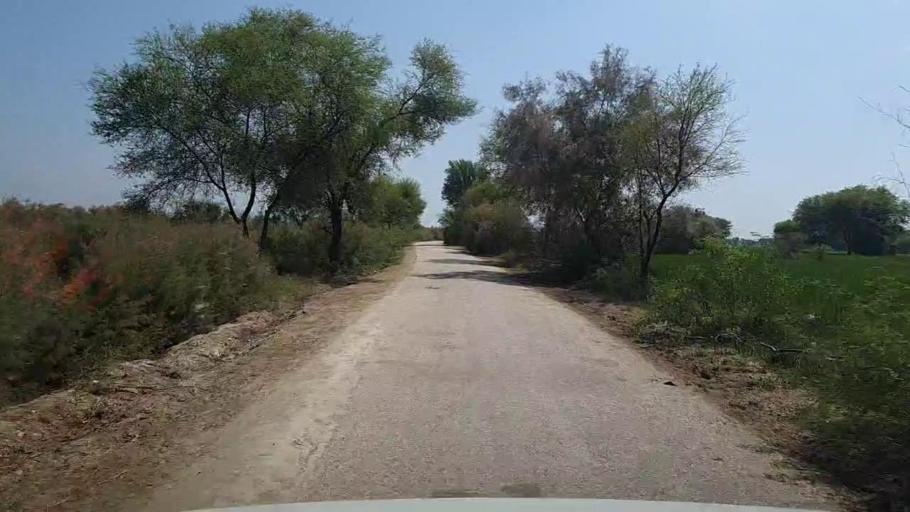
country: PK
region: Sindh
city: Kandhkot
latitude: 28.2828
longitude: 69.3548
